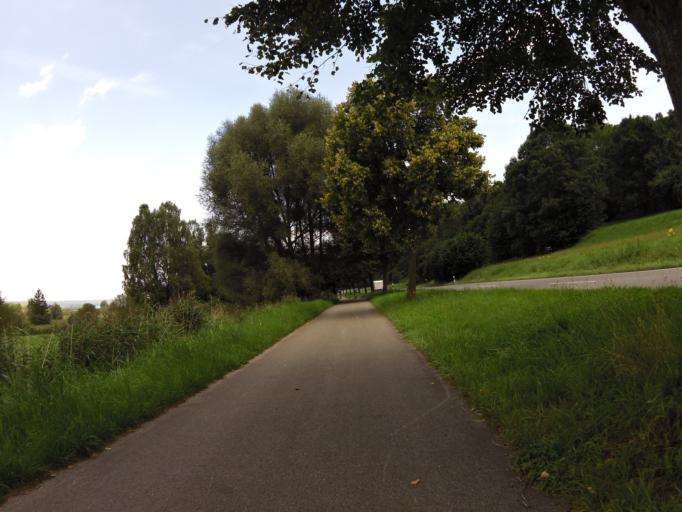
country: DE
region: Bavaria
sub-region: Upper Bavaria
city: Pahl
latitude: 47.9359
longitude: 11.1535
